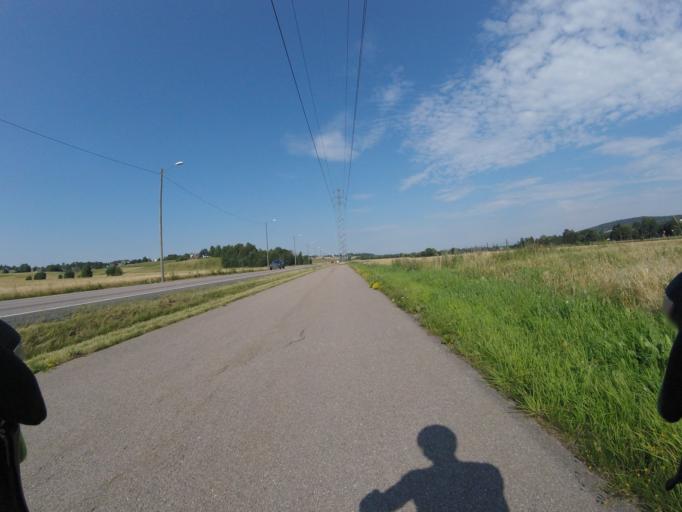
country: NO
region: Akershus
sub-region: Skedsmo
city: Leirsund
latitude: 59.9804
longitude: 11.0698
